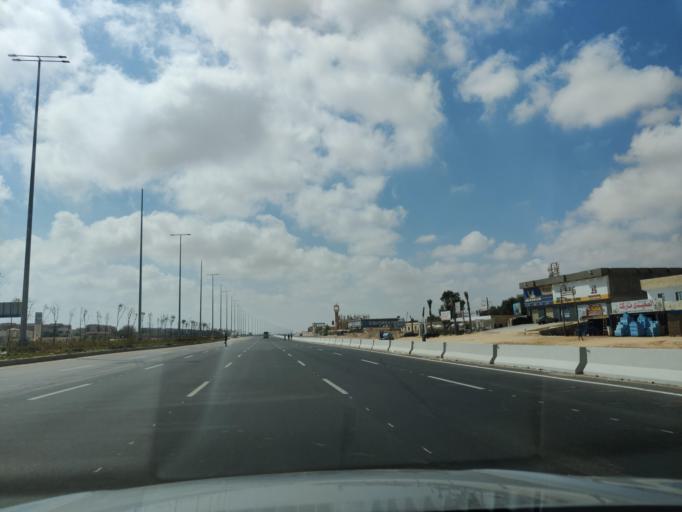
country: EG
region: Muhafazat Matruh
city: Al `Alamayn
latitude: 30.9433
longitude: 28.7799
